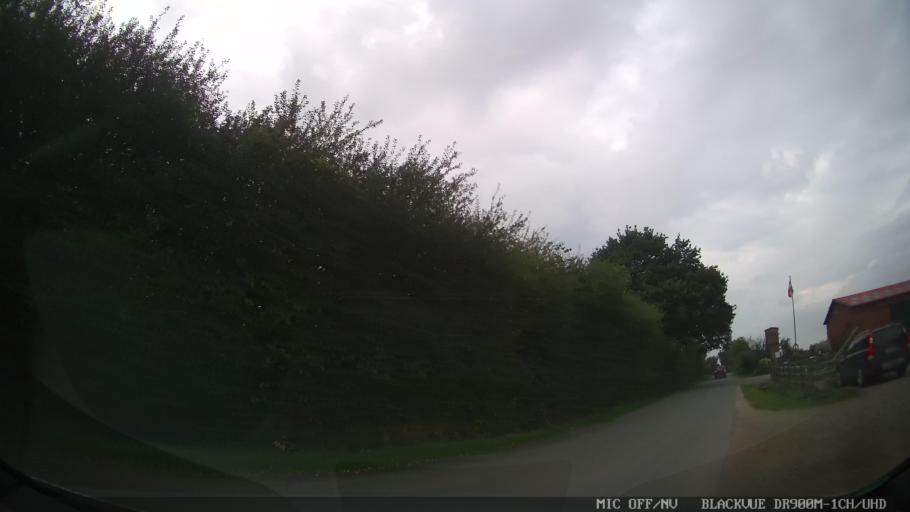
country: DE
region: Schleswig-Holstein
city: Gromitz
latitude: 54.1835
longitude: 10.9512
